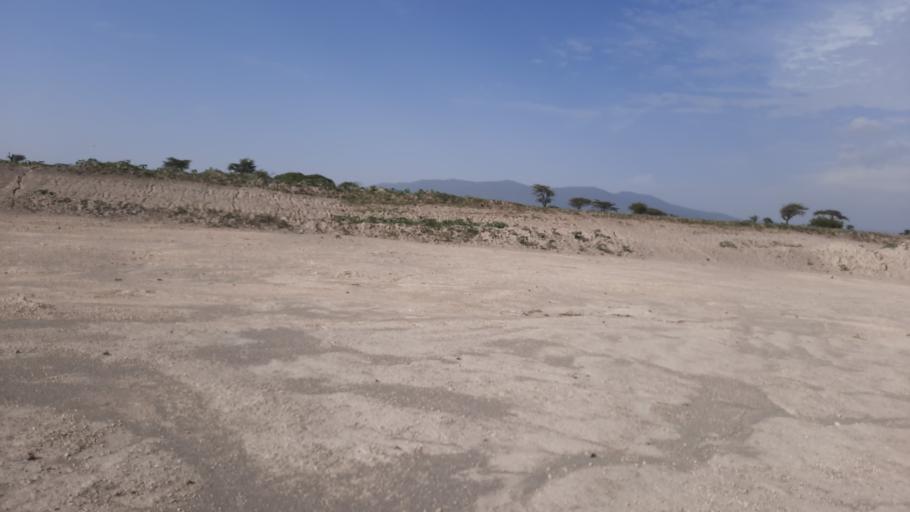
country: ET
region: Oromiya
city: Ziway
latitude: 7.6928
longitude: 38.6642
